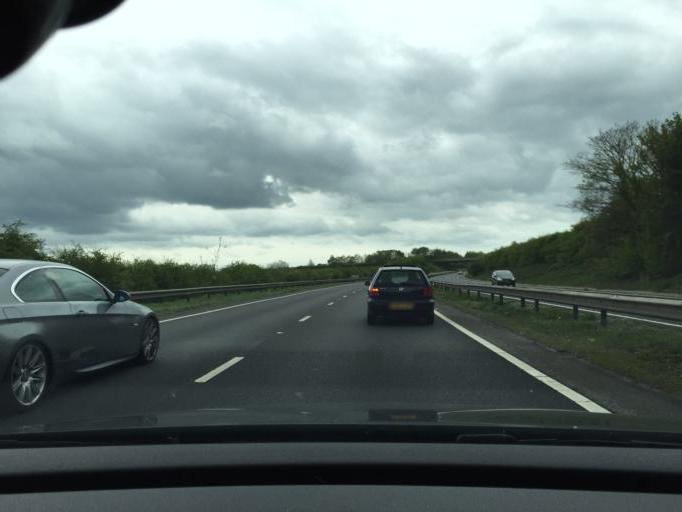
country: GB
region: England
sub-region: Oxfordshire
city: Harwell
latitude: 51.5951
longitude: -1.2785
